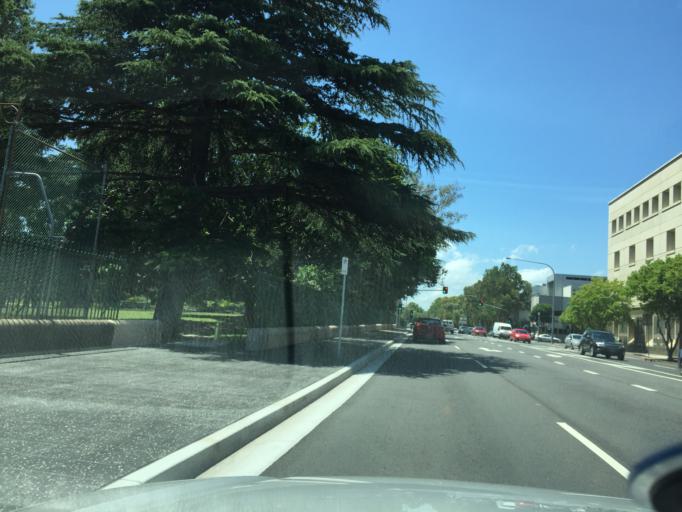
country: AU
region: New South Wales
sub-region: Parramatta
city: City of Parramatta
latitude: -33.8138
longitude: 151.0000
